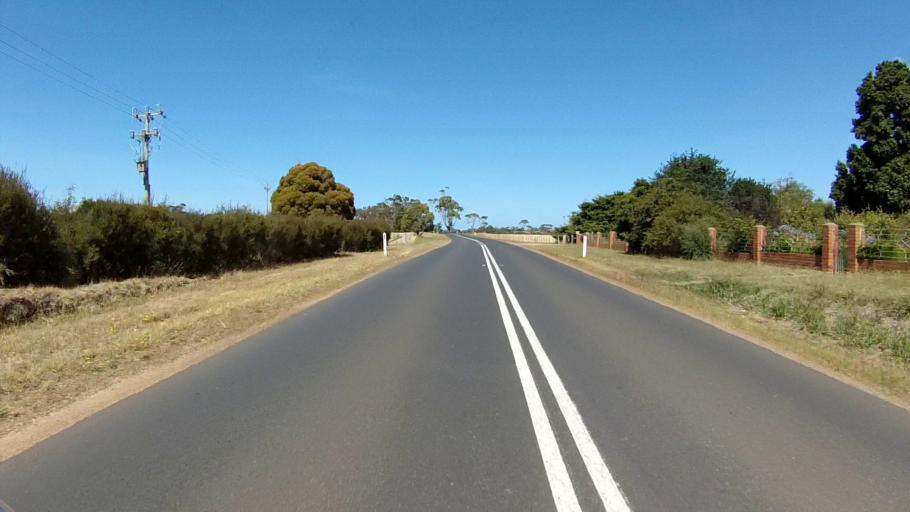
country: AU
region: Tasmania
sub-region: Break O'Day
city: St Helens
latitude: -42.1167
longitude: 148.0617
